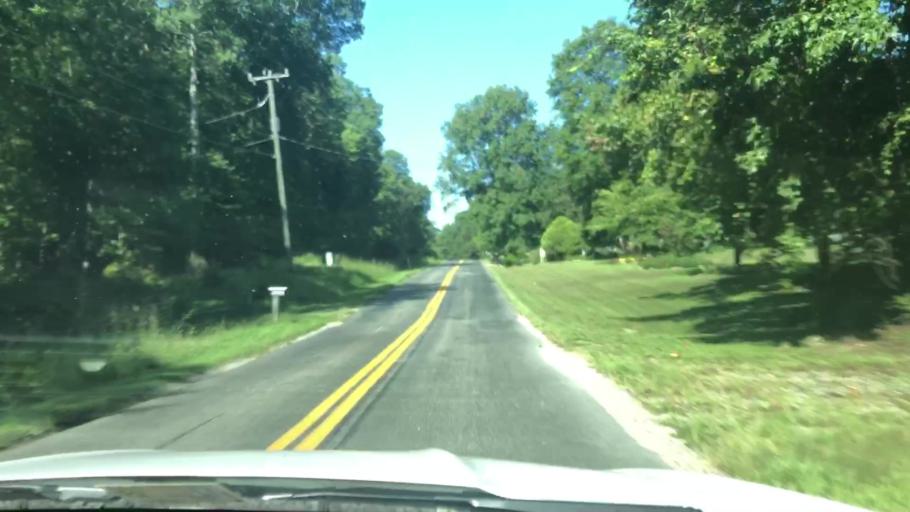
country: US
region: Virginia
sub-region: New Kent County
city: New Kent
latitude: 37.4186
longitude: -76.9185
